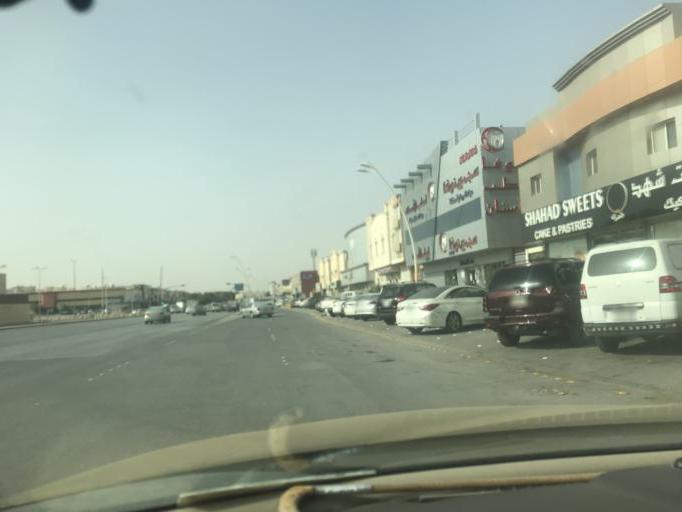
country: SA
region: Ar Riyad
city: Riyadh
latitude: 24.6815
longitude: 46.7988
